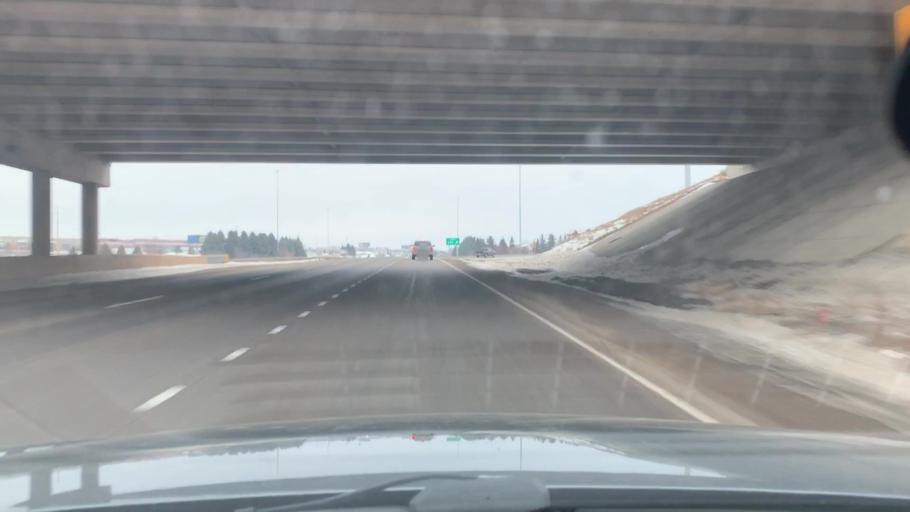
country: US
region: North Dakota
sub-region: Burleigh County
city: Bismarck
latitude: 46.8275
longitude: -100.8160
